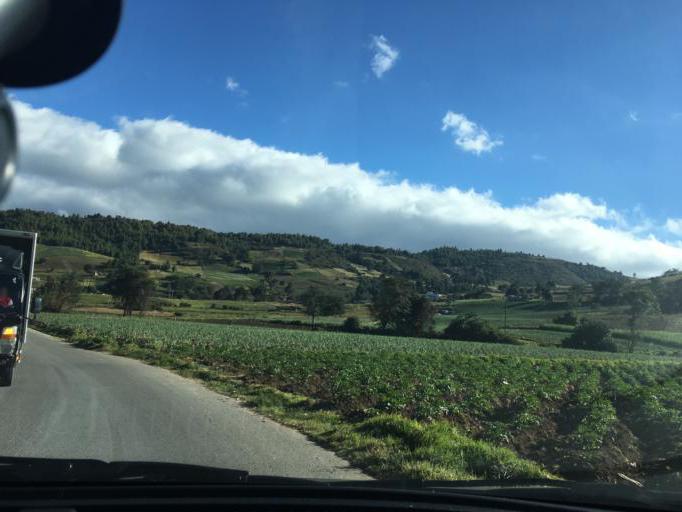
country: CO
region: Boyaca
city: Pesca
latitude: 5.5143
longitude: -72.9763
